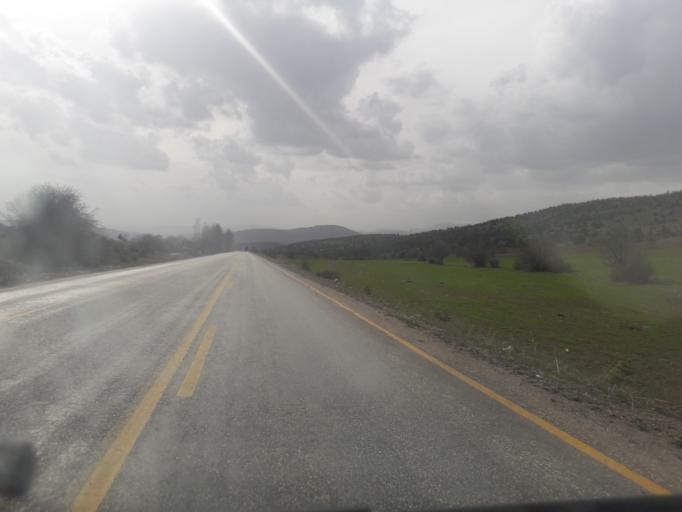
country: TR
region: Gumushane
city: Evren
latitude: 40.1692
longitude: 39.2727
